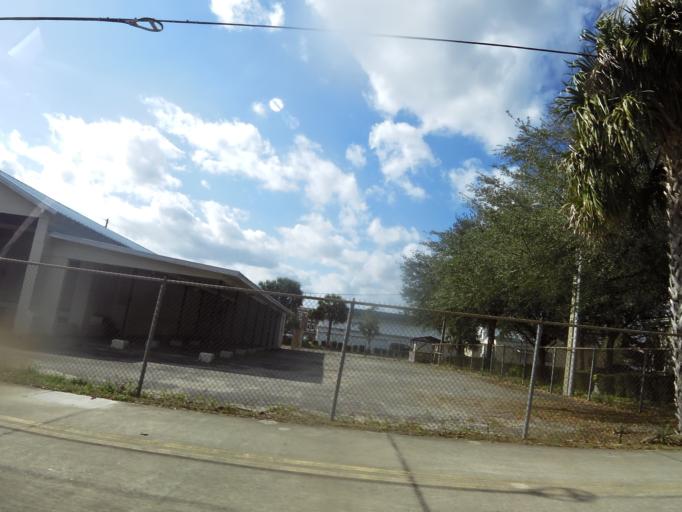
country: US
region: Florida
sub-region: Volusia County
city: DeLand
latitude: 29.0276
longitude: -81.3014
